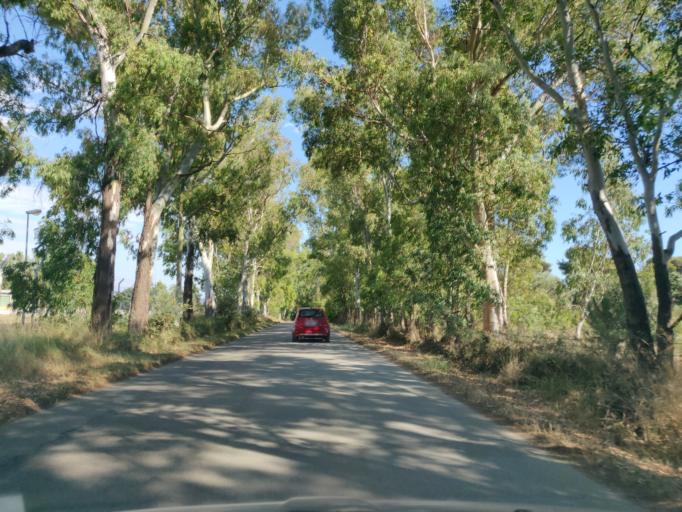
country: IT
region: Latium
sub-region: Citta metropolitana di Roma Capitale
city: Aurelia
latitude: 42.1646
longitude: 11.7430
